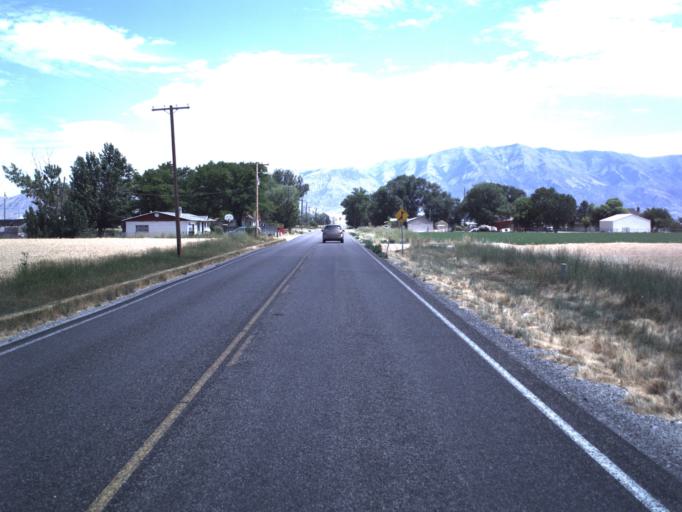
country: US
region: Utah
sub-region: Box Elder County
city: Tremonton
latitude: 41.7104
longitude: -112.2241
